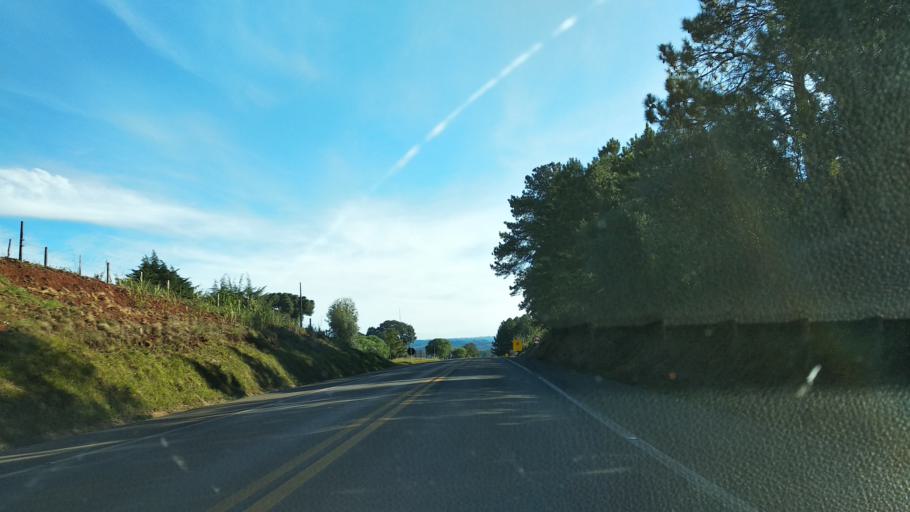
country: BR
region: Santa Catarina
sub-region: Celso Ramos
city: Celso Ramos
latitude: -27.5286
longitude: -51.3832
